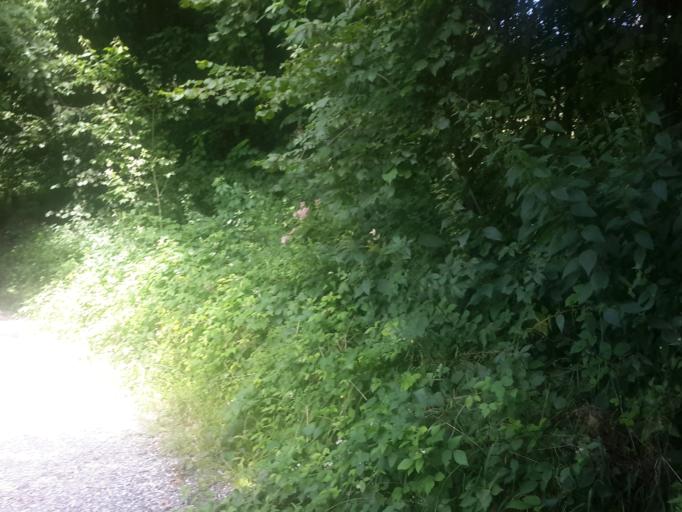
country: AT
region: Tyrol
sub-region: Politischer Bezirk Kufstein
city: Kufstein
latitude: 47.5909
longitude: 12.1529
